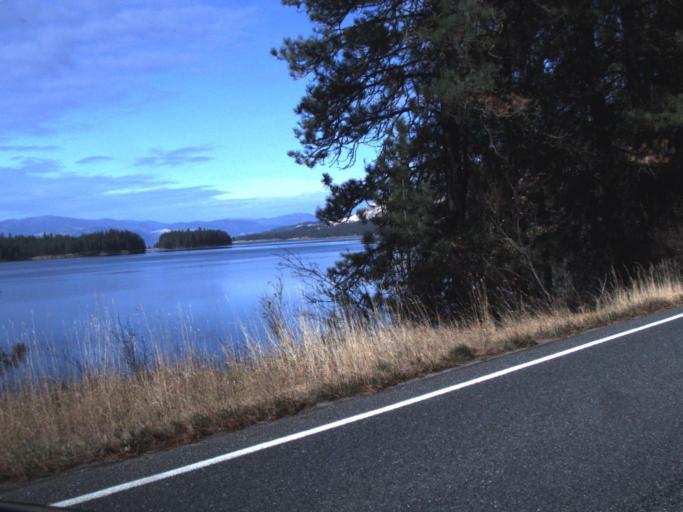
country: US
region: Washington
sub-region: Stevens County
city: Kettle Falls
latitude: 48.2464
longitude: -118.1395
